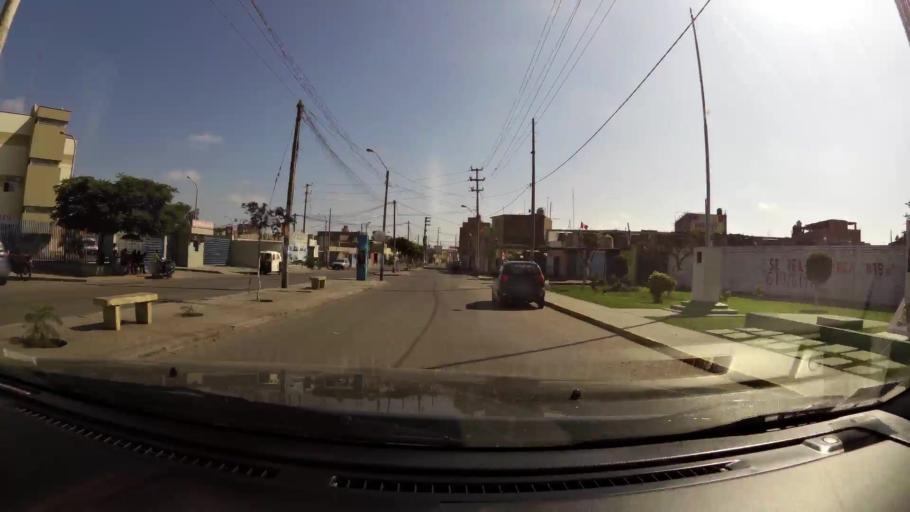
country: PE
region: Ica
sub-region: Provincia de Chincha
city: Chincha Alta
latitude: -13.4238
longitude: -76.1328
